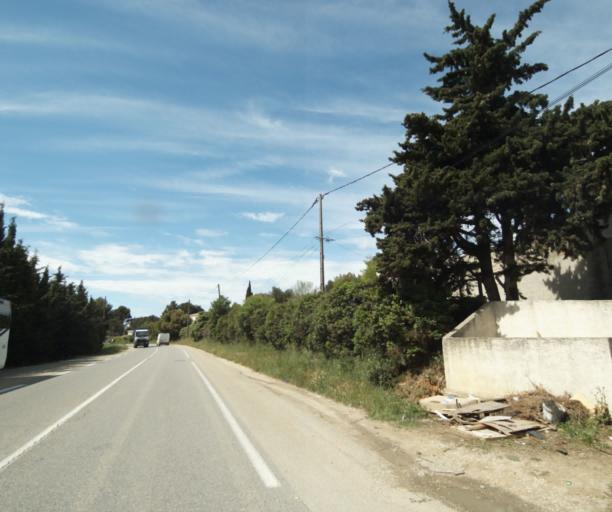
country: FR
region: Provence-Alpes-Cote d'Azur
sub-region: Departement des Bouches-du-Rhone
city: Rognac
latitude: 43.5121
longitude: 5.2269
